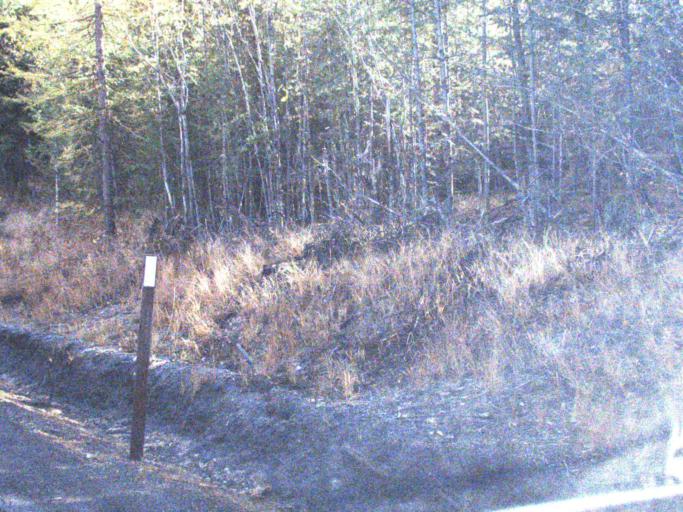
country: US
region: Washington
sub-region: Ferry County
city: Republic
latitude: 48.6140
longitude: -118.5571
